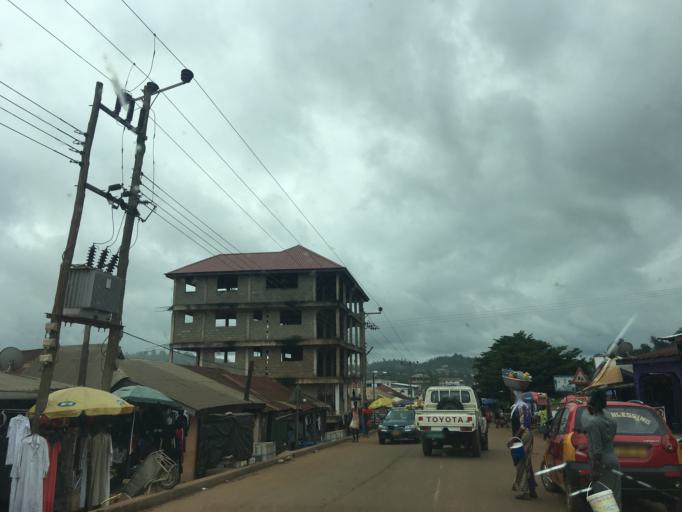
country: GH
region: Western
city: Wassa-Akropong
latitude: 5.8086
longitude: -2.4362
